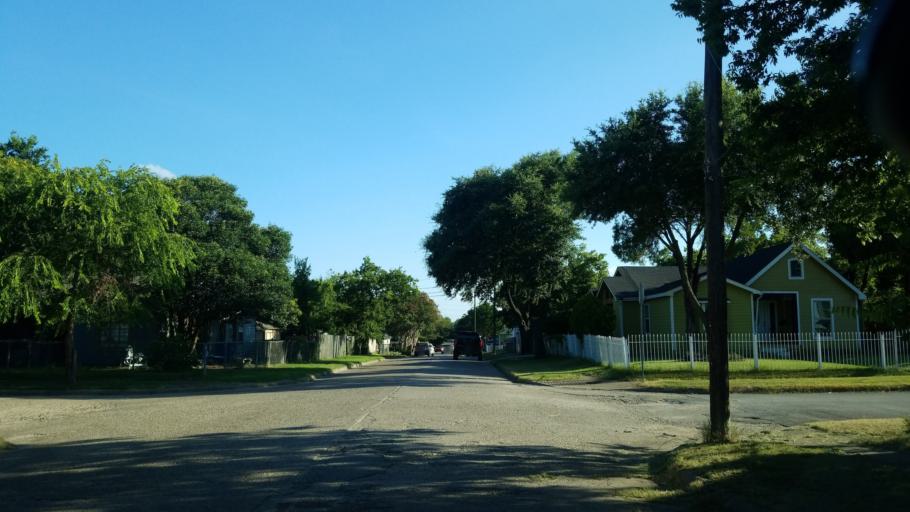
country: US
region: Texas
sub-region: Dallas County
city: Dallas
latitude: 32.7775
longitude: -96.7111
